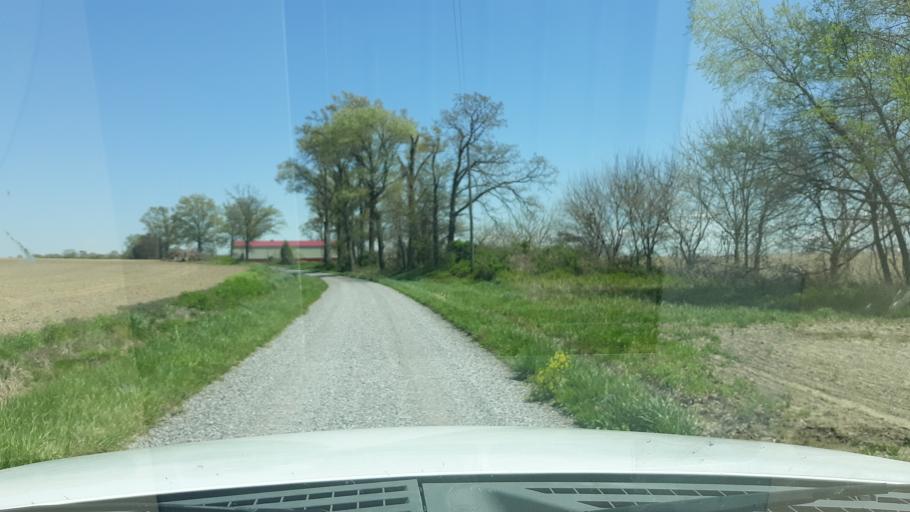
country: US
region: Illinois
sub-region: Saline County
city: Harrisburg
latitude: 37.8889
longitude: -88.6764
